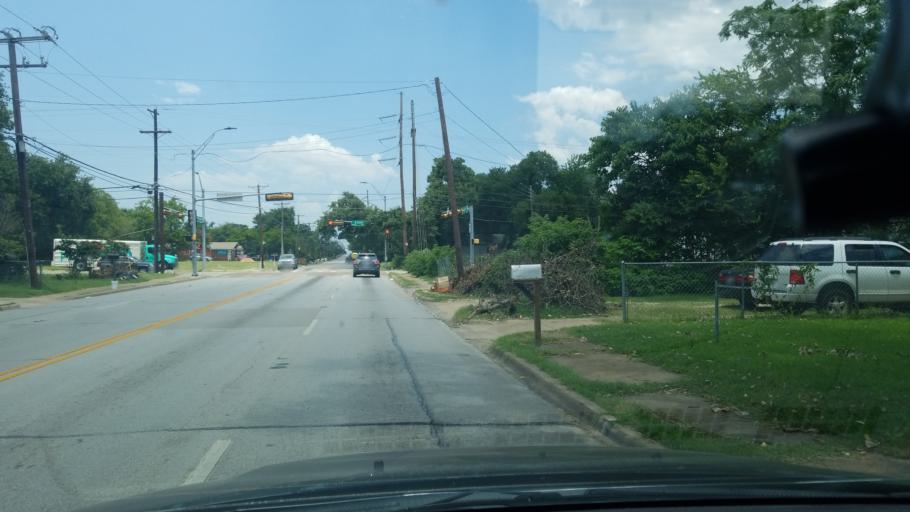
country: US
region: Texas
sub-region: Dallas County
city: Balch Springs
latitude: 32.7189
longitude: -96.6571
